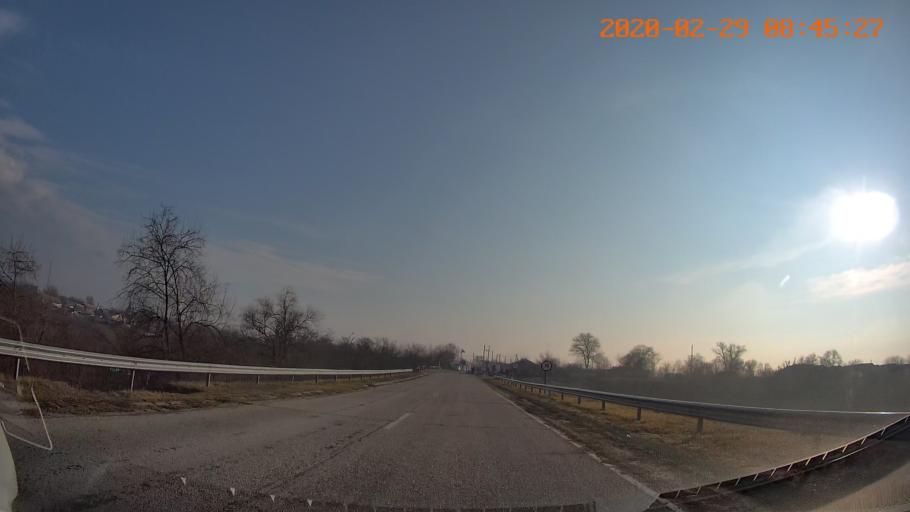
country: MD
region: Anenii Noi
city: Varnita
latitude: 46.9195
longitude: 29.4786
